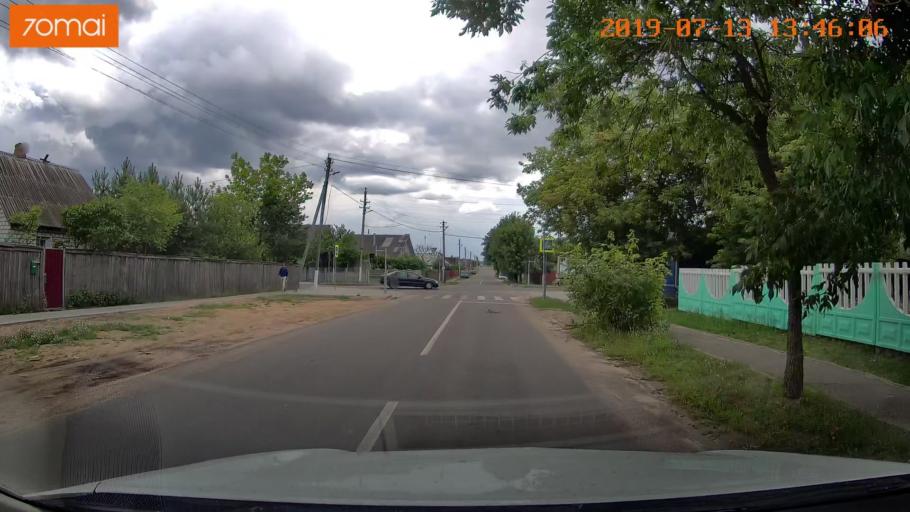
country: BY
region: Mogilev
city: Asipovichy
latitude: 53.2963
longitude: 28.6309
